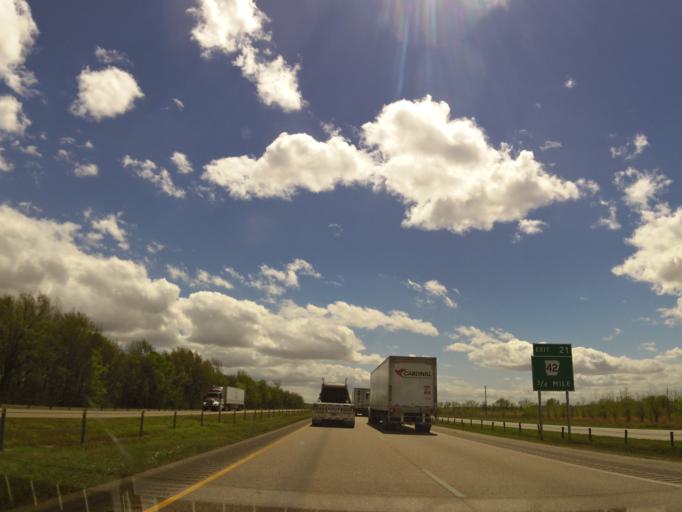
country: US
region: Arkansas
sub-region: Crittenden County
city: Marion
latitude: 35.3813
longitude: -90.2795
